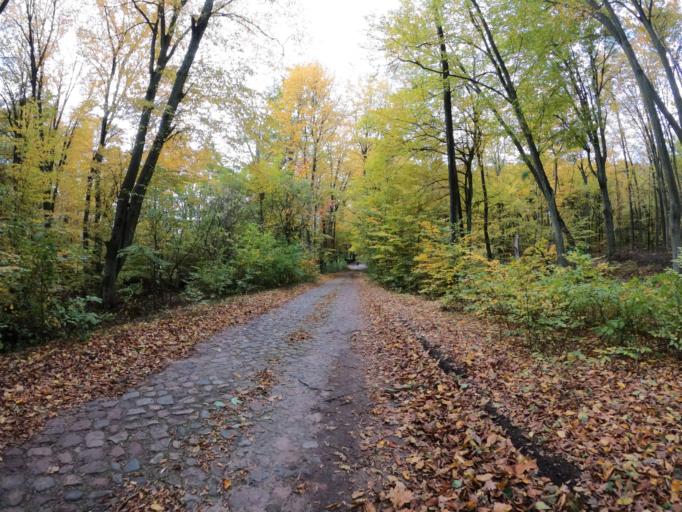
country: PL
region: West Pomeranian Voivodeship
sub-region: Powiat mysliborski
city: Barlinek
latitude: 52.9082
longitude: 15.2751
